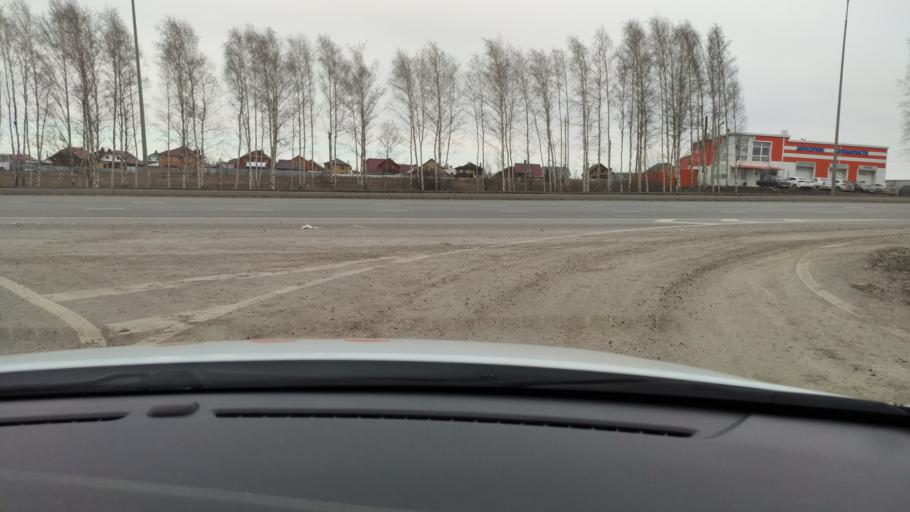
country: RU
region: Tatarstan
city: Vysokaya Gora
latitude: 55.8018
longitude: 49.2845
